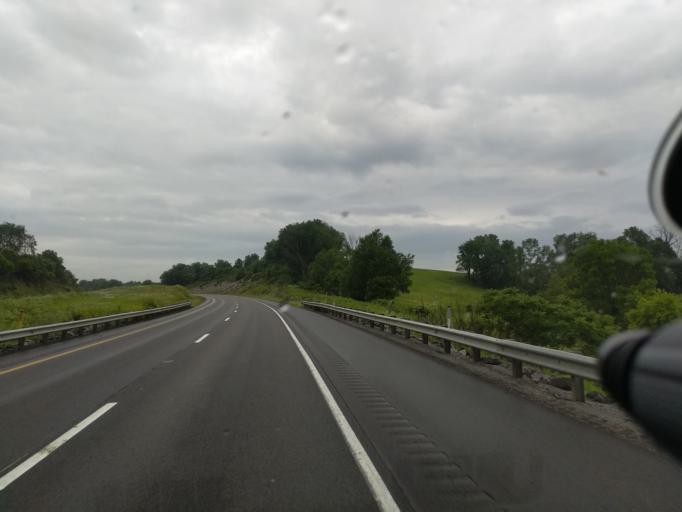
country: US
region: Pennsylvania
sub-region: Northumberland County
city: Milton
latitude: 41.0408
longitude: -76.8118
